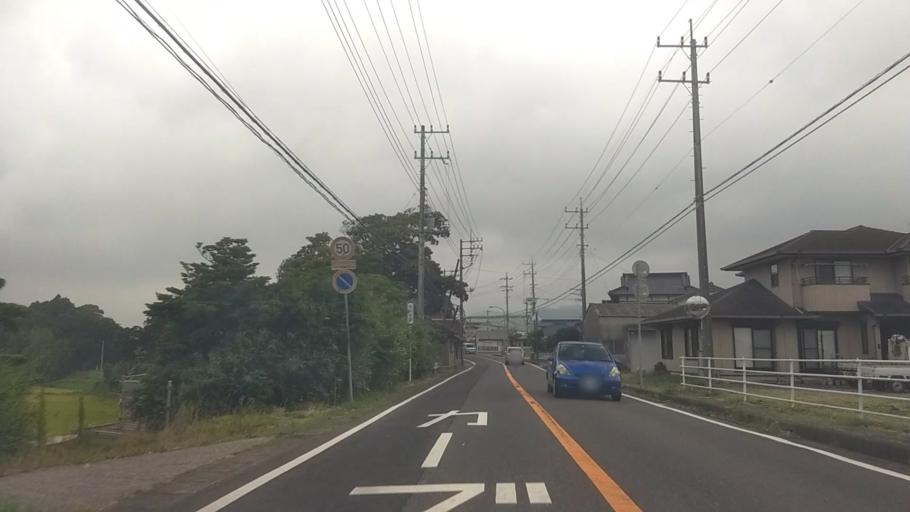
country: JP
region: Chiba
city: Kawaguchi
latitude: 35.1254
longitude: 140.0587
